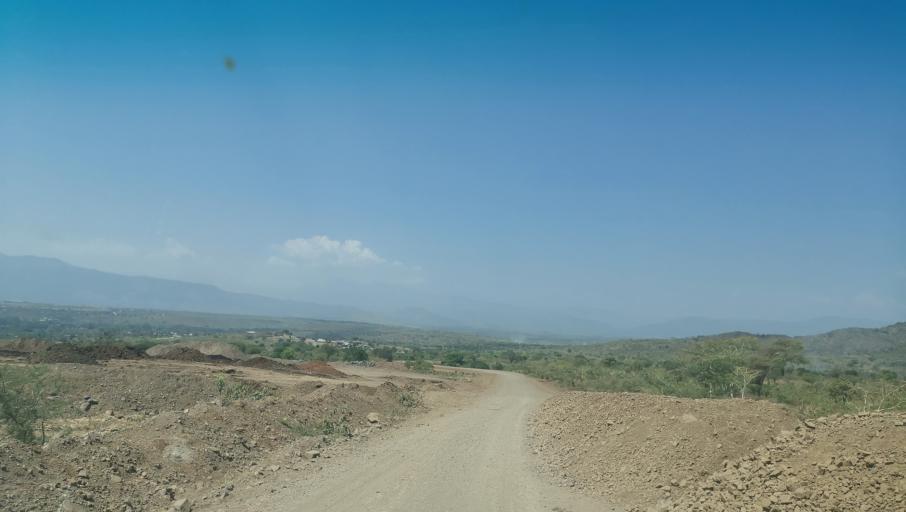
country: ET
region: Southern Nations, Nationalities, and People's Region
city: Arba Minch'
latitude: 6.3362
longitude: 37.3273
